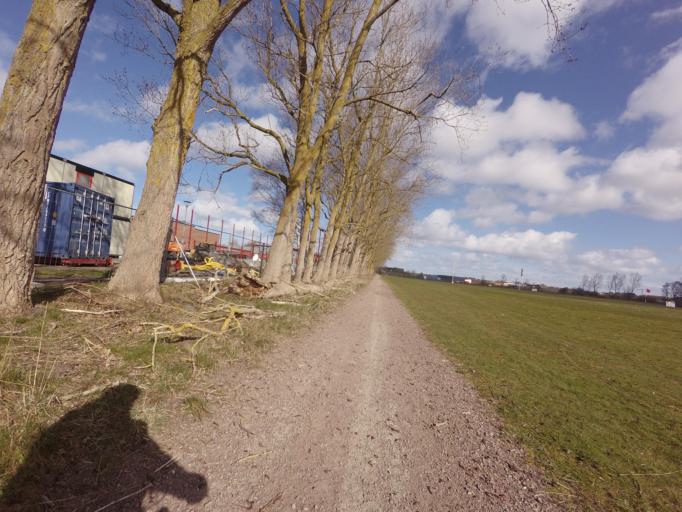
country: SE
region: Skane
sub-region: Hoganas Kommun
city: Hoganas
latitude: 56.1855
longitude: 12.5675
